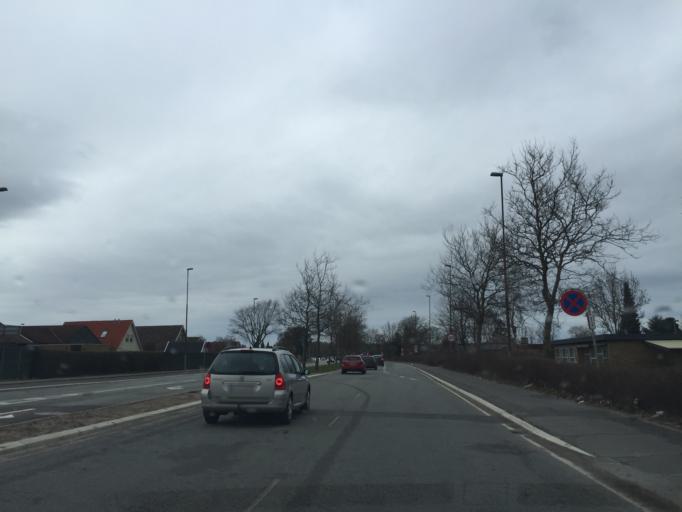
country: DK
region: South Denmark
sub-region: Odense Kommune
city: Odense
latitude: 55.4104
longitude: 10.3405
